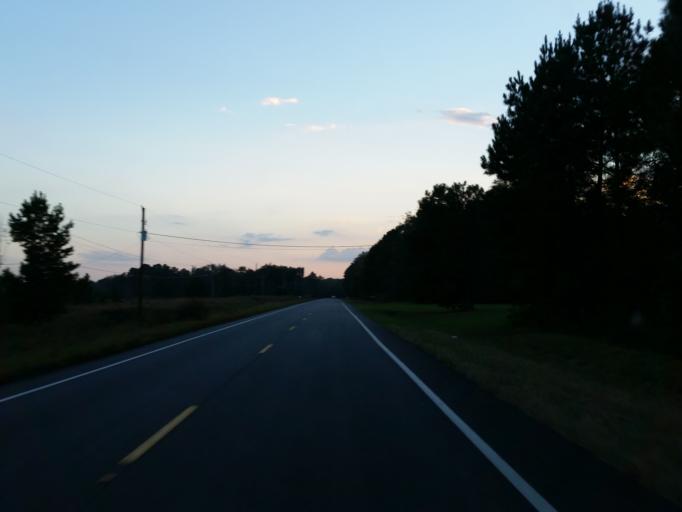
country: US
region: Georgia
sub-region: Pulaski County
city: Hawkinsville
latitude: 32.2476
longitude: -83.4968
